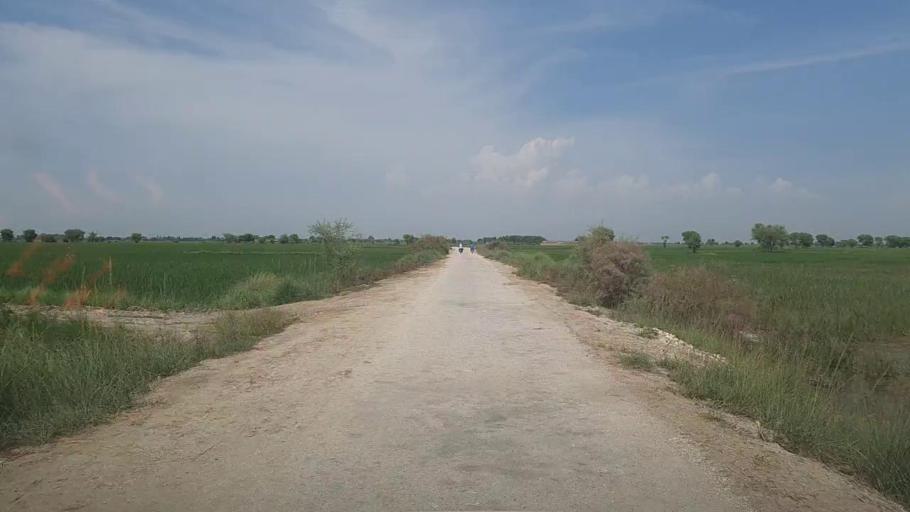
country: PK
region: Sindh
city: Kandhkot
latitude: 28.2824
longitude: 69.2379
